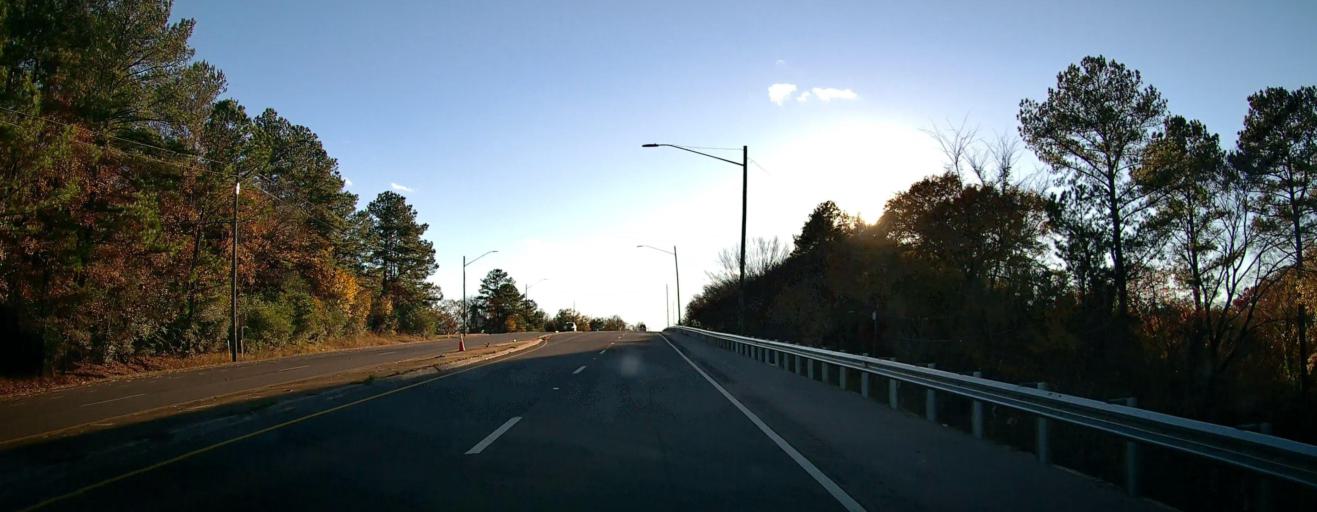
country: US
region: Alabama
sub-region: Jefferson County
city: Fultondale
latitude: 33.5671
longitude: -86.8151
